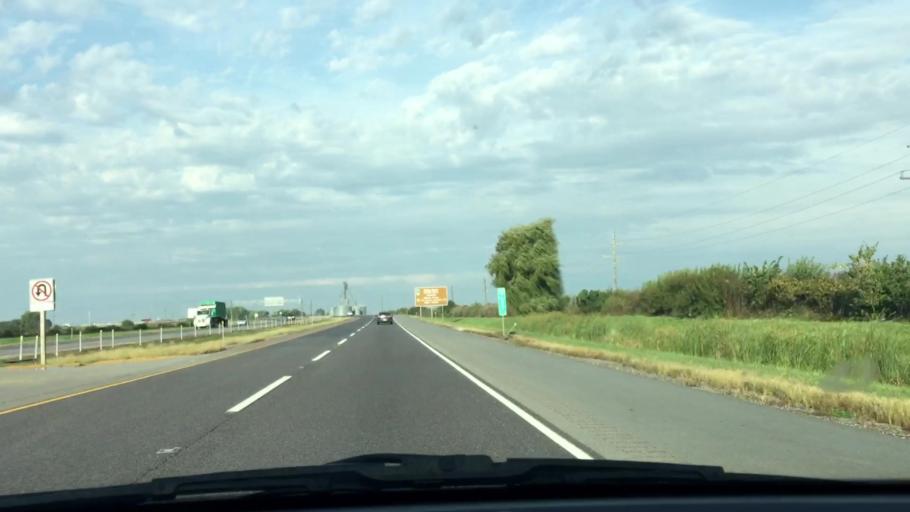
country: US
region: Illinois
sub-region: Lee County
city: Dixon
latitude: 41.8250
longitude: -89.4457
